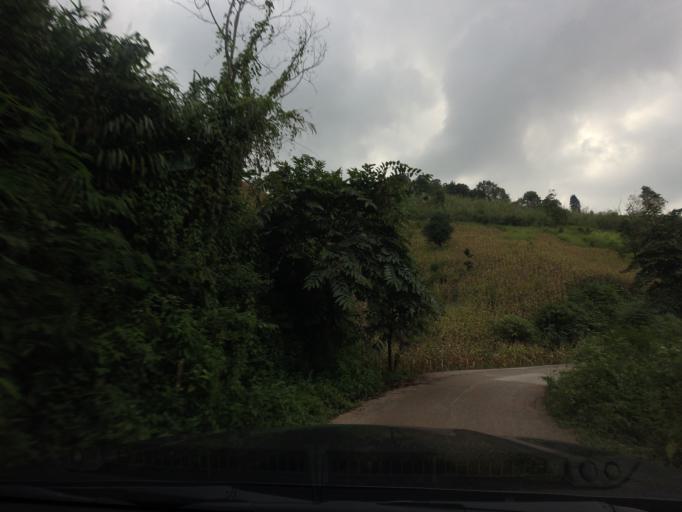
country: TH
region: Nan
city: Bo Kluea
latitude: 19.3509
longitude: 101.1694
